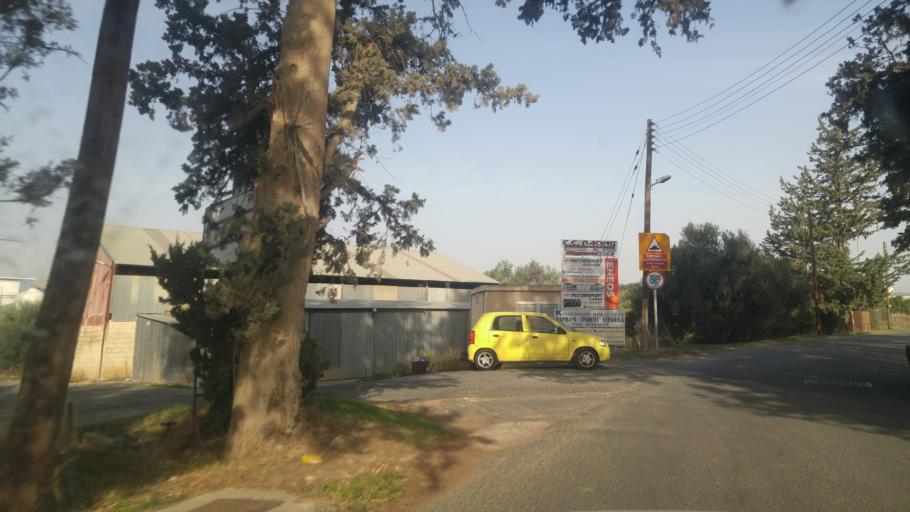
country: CY
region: Limassol
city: Pano Polemidia
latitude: 34.6647
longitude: 32.9982
